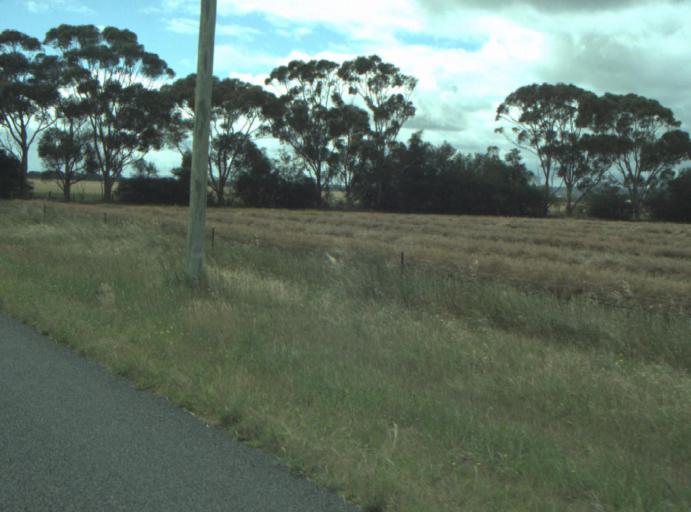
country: AU
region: Victoria
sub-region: Greater Geelong
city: Lara
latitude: -37.8567
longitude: 144.3632
